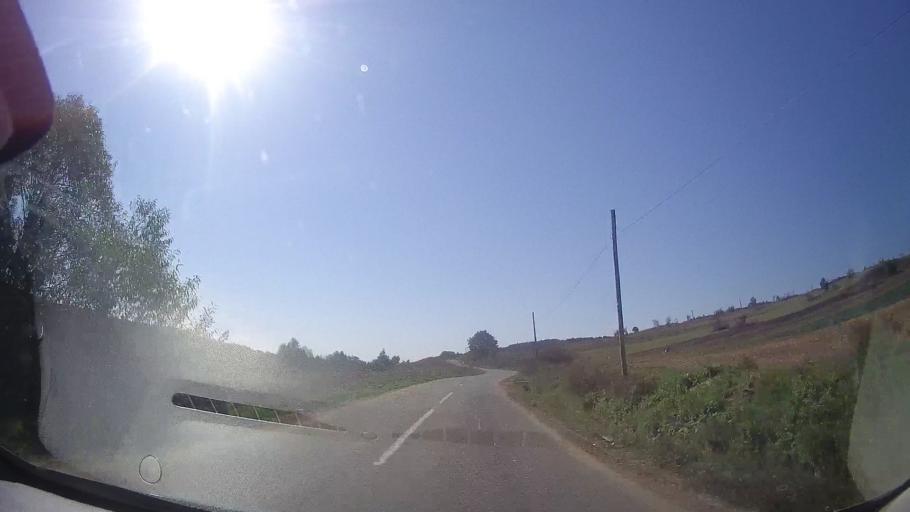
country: RO
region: Timis
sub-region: Comuna Ohaba Lunga
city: Ohaba Lunga
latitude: 45.8972
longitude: 21.9736
